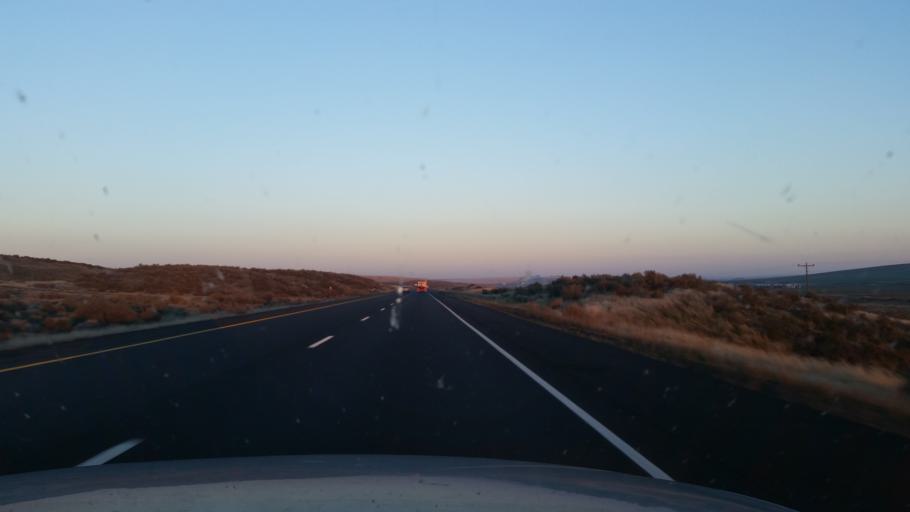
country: US
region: Washington
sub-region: Grant County
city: Warden
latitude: 47.0863
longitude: -118.9347
